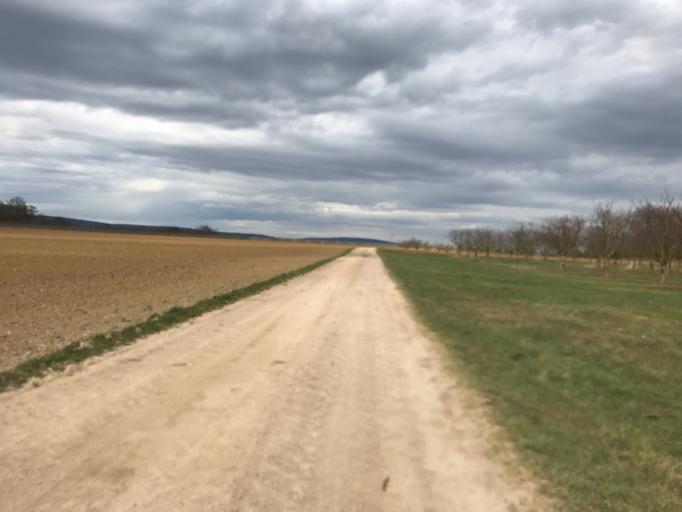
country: DE
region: Rheinland-Pfalz
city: Wackernheim
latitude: 49.9583
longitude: 8.1047
